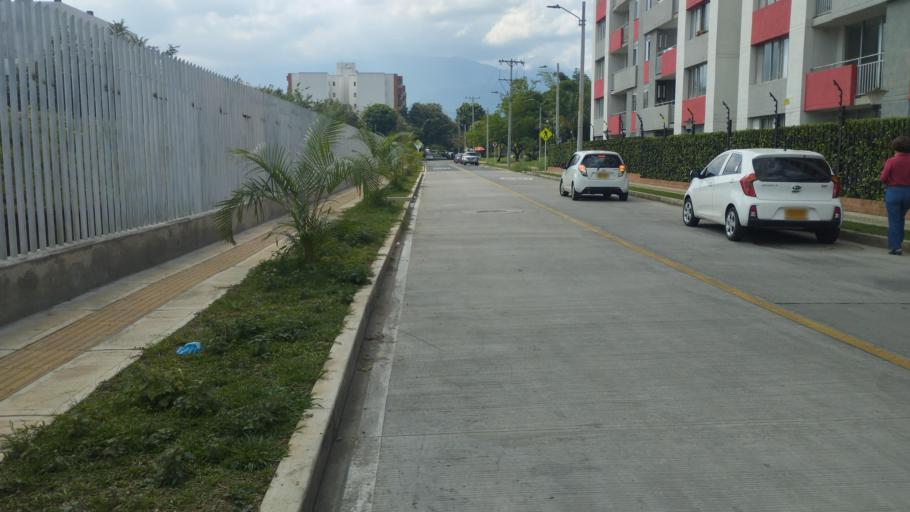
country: CO
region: Valle del Cauca
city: Cali
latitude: 3.3940
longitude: -76.5248
